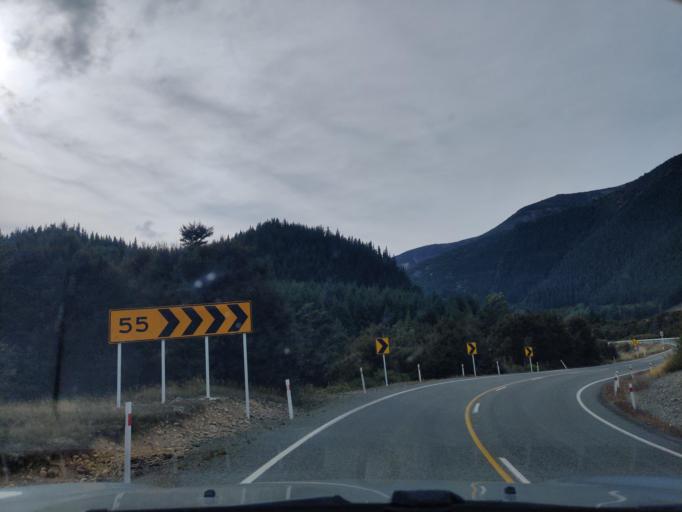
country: NZ
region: Tasman
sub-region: Tasman District
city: Wakefield
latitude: -41.7141
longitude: 173.0908
